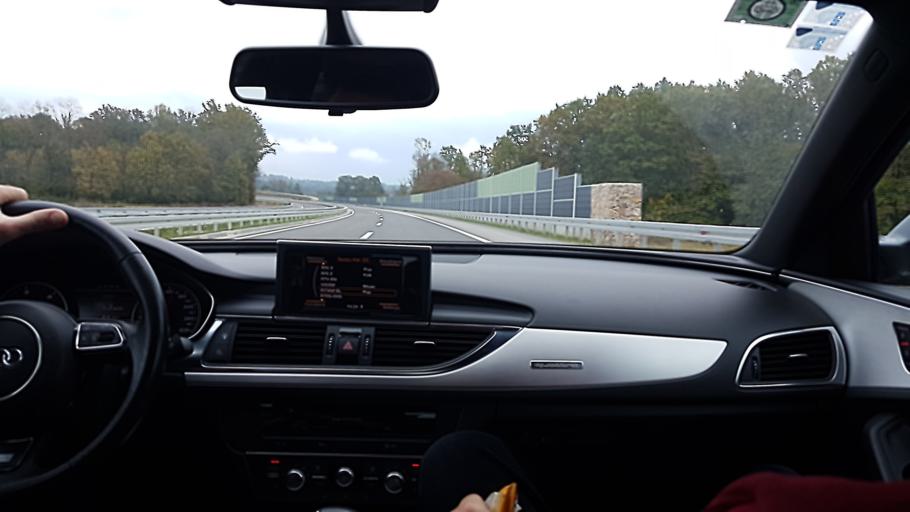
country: BA
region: Republika Srpska
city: Stanari
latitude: 44.8444
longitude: 17.7803
